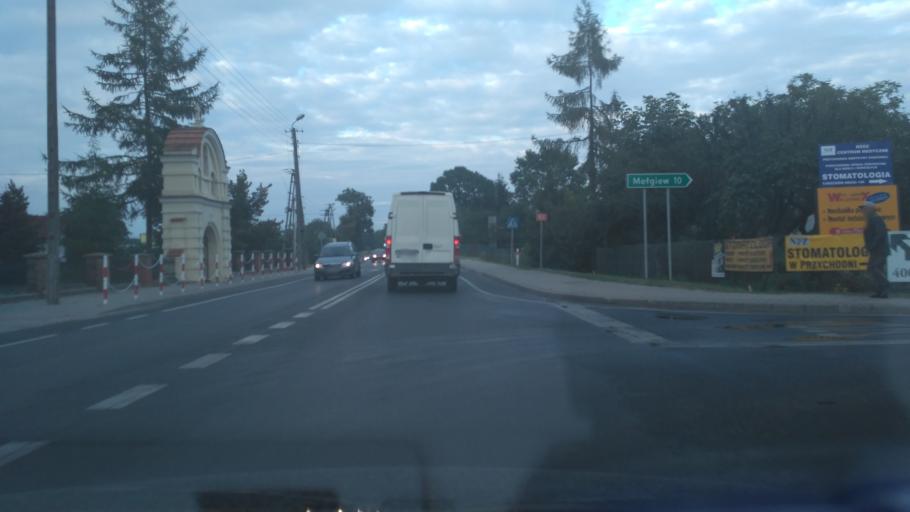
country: PL
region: Lublin Voivodeship
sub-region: Powiat leczynski
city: Spiczyn
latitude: 51.3020
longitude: 22.7272
